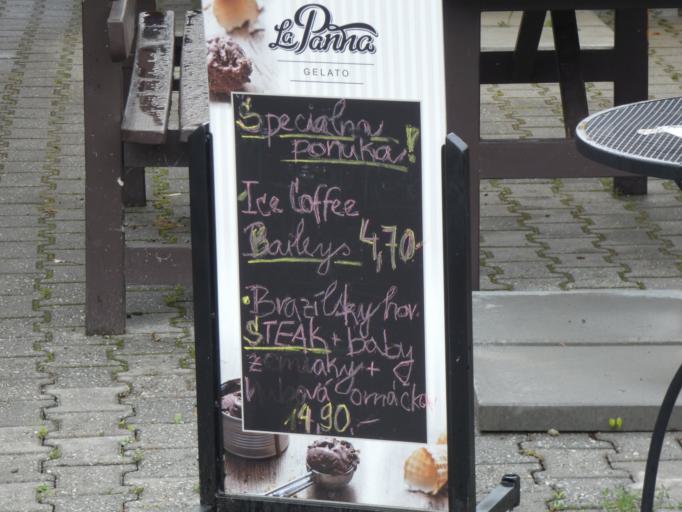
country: AT
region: Lower Austria
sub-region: Politischer Bezirk Bruck an der Leitha
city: Hainburg an der Donau
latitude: 48.1753
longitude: 16.9788
